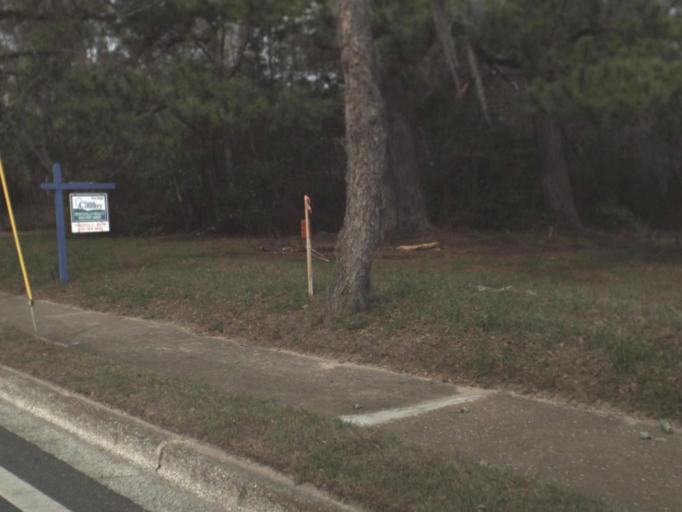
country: US
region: Florida
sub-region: Jefferson County
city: Monticello
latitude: 30.5362
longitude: -83.8702
